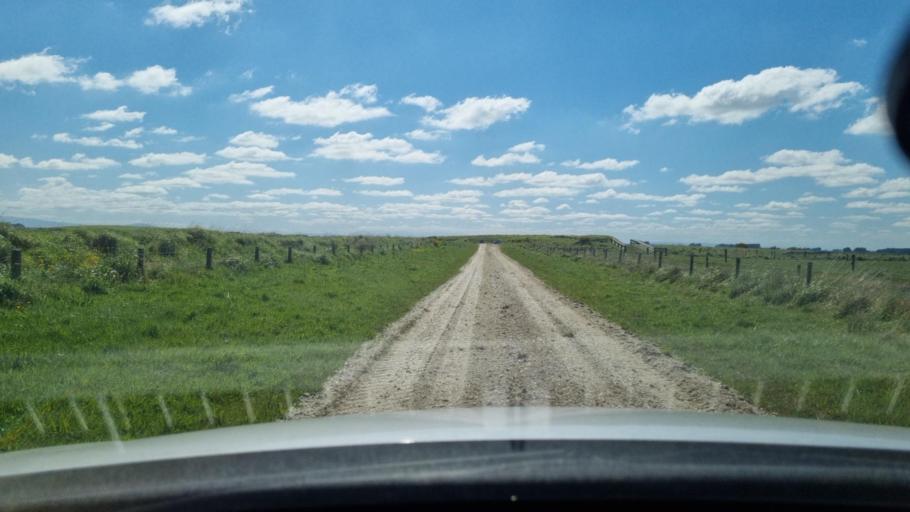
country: NZ
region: Southland
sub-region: Invercargill City
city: Invercargill
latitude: -46.3871
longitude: 168.2581
